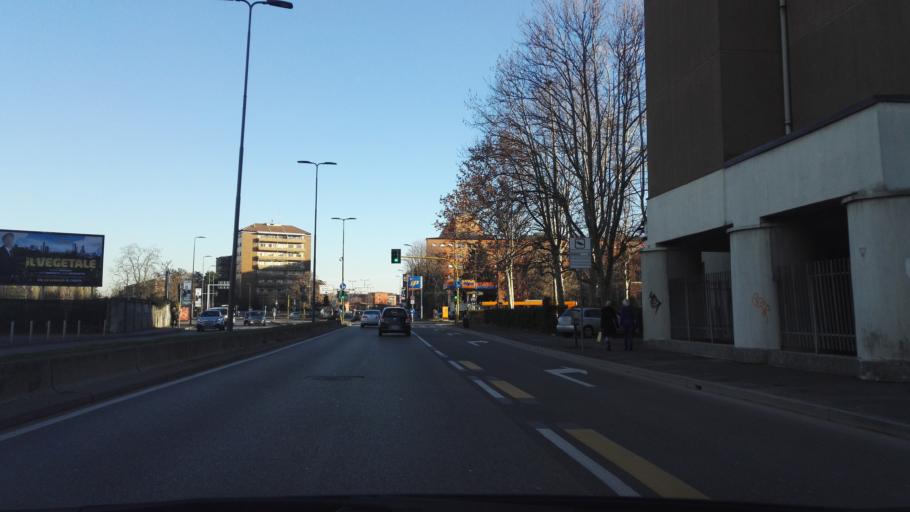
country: IT
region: Lombardy
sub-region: Citta metropolitana di Milano
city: Figino
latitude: 45.4768
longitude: 9.1105
